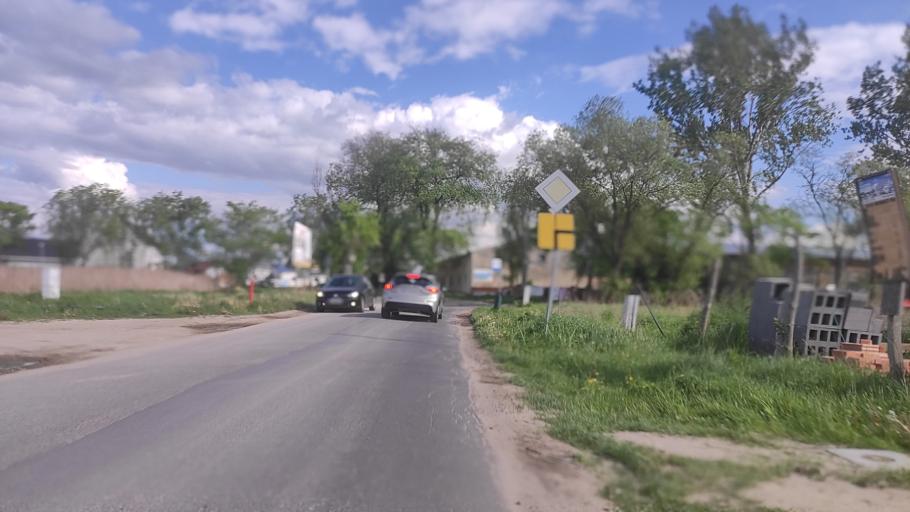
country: PL
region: Greater Poland Voivodeship
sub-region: Powiat poznanski
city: Swarzedz
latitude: 52.3909
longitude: 17.1189
